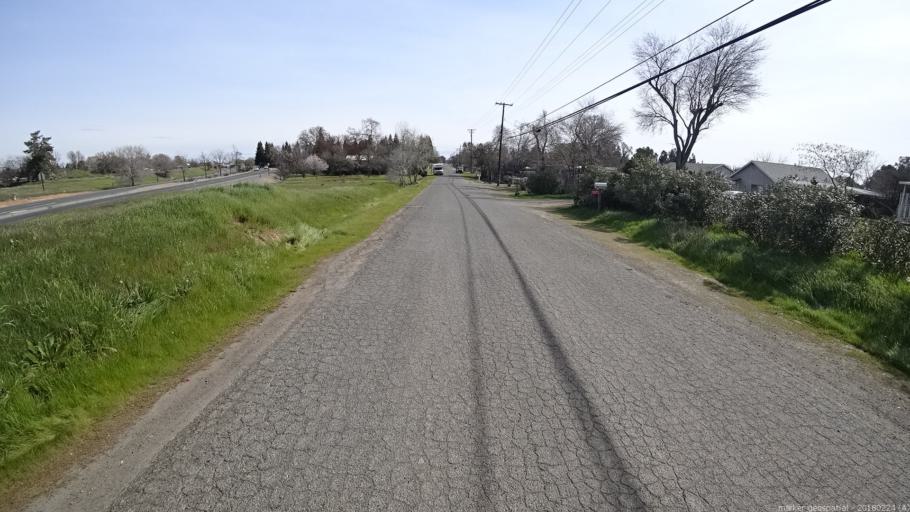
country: US
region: California
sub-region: Sacramento County
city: Rio Linda
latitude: 38.6837
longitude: -121.4371
